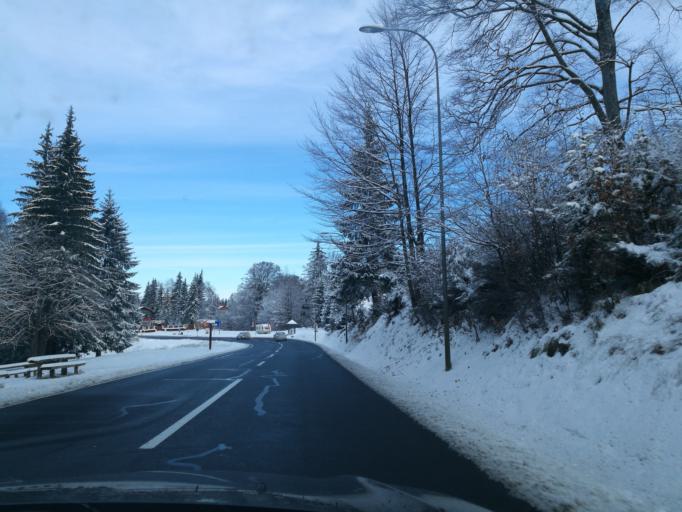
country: RO
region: Brasov
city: Brasov
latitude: 45.6066
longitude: 25.5543
